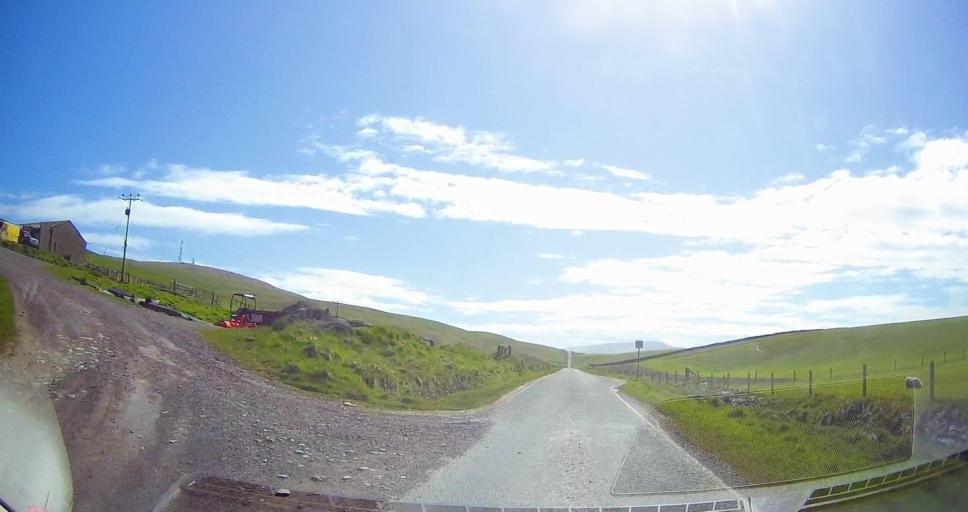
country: GB
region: Scotland
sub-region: Shetland Islands
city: Sandwick
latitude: 59.9695
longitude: -1.3178
